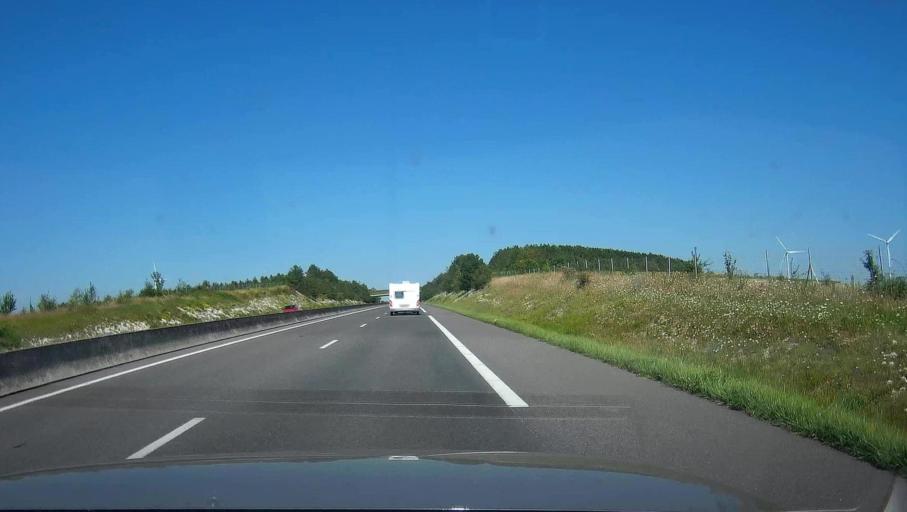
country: FR
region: Champagne-Ardenne
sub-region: Departement de l'Aube
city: Arcis-sur-Aube
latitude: 48.5740
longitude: 4.1902
